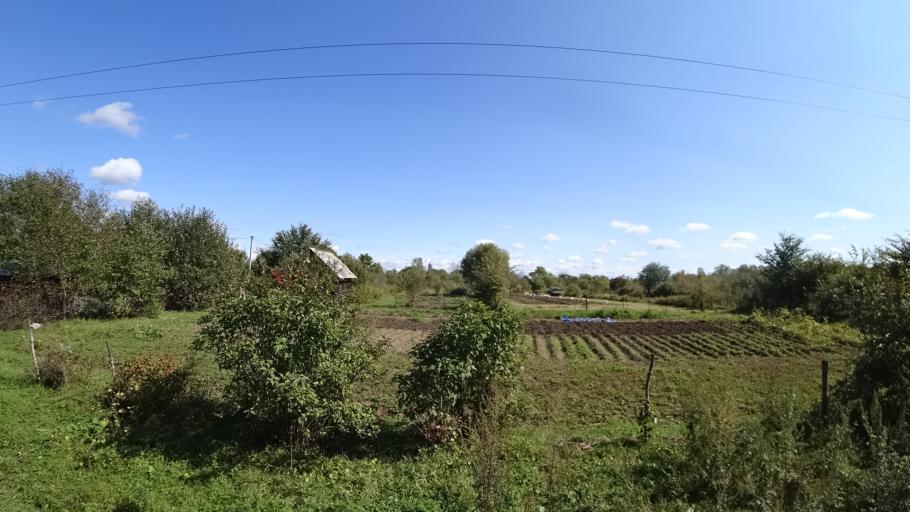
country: RU
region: Amur
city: Arkhara
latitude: 49.3997
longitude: 130.1263
